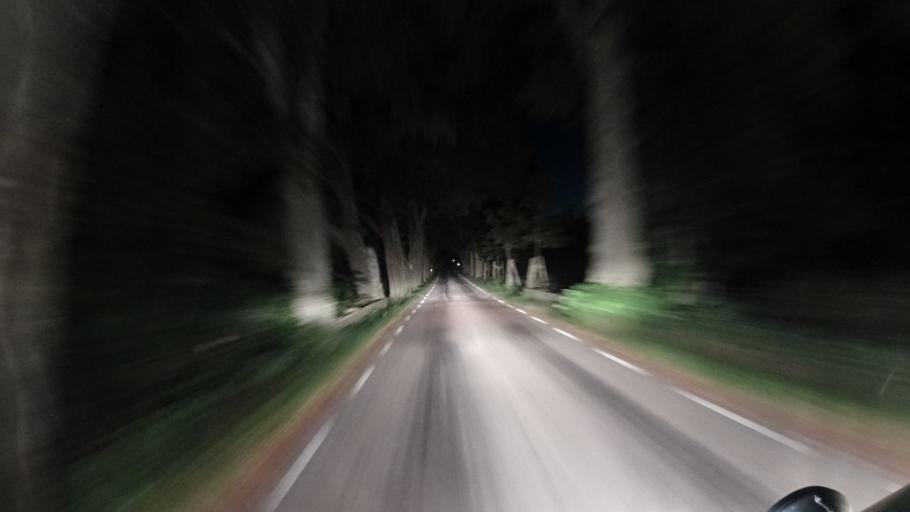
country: SE
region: OEstergoetland
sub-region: Vadstena Kommun
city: Herrestad
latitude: 58.3184
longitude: 14.8423
